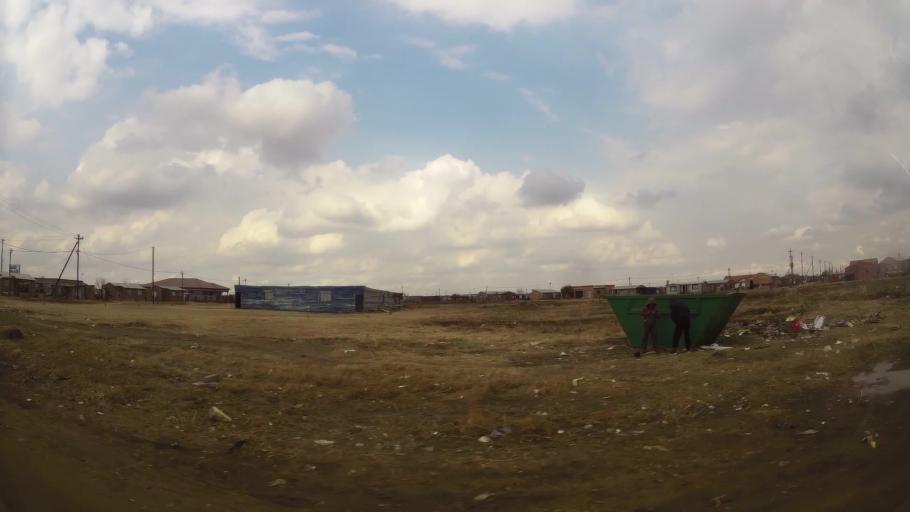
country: ZA
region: Orange Free State
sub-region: Fezile Dabi District Municipality
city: Sasolburg
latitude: -26.8587
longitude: 27.8927
